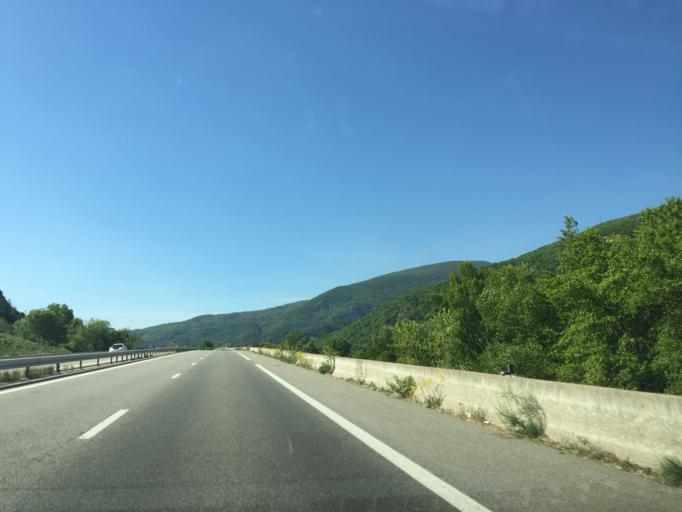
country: FR
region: Provence-Alpes-Cote d'Azur
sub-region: Departement des Alpes-de-Haute-Provence
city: Sisteron
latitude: 44.1772
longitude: 5.9543
